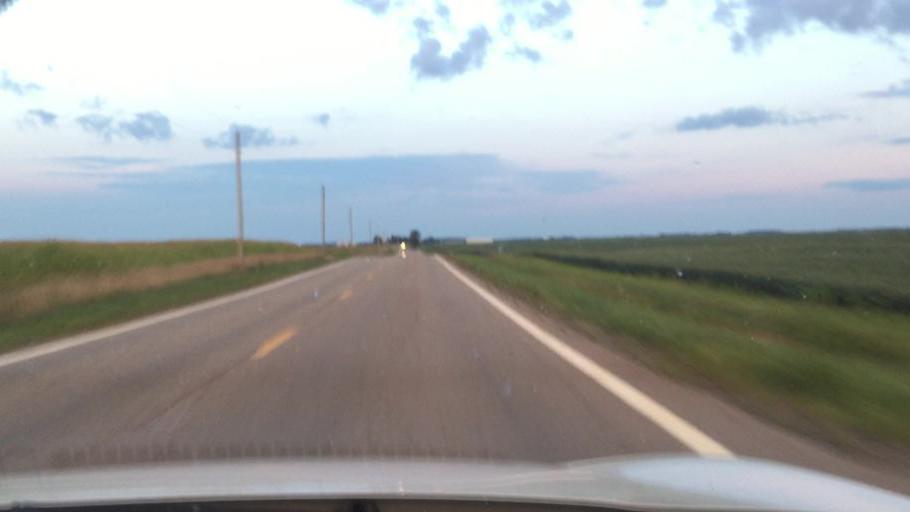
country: US
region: Ohio
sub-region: Madison County
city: Choctaw Lake
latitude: 40.0119
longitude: -83.4551
